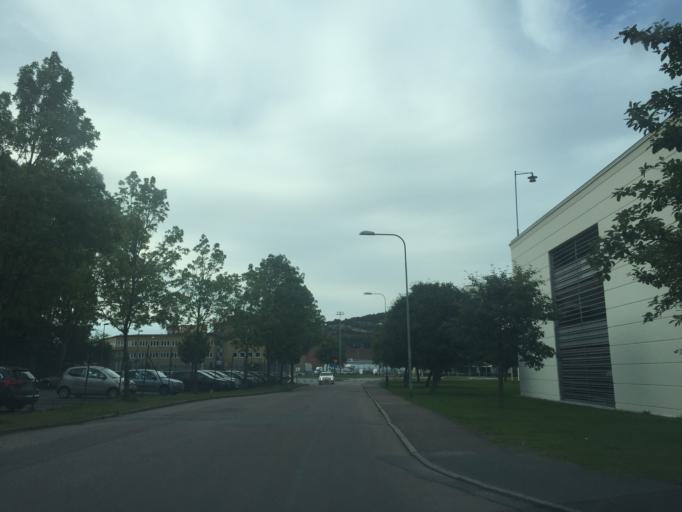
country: SE
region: Vaestra Goetaland
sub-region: Goteborg
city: Majorna
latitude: 57.7066
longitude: 11.9348
